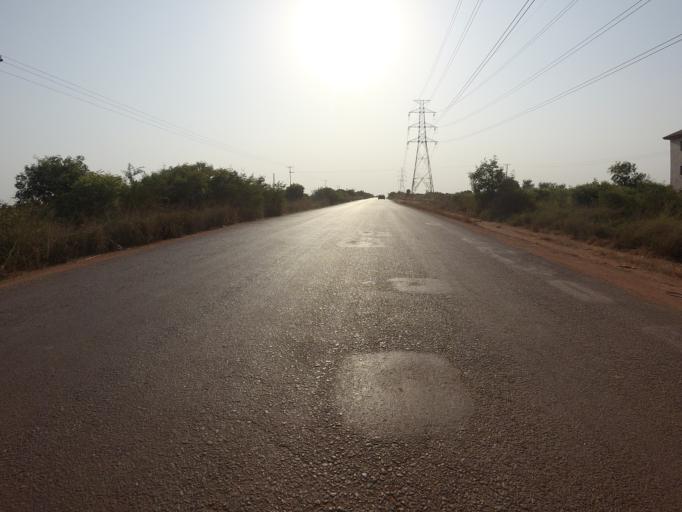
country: GH
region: Greater Accra
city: Tema
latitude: 5.6777
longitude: 0.0361
